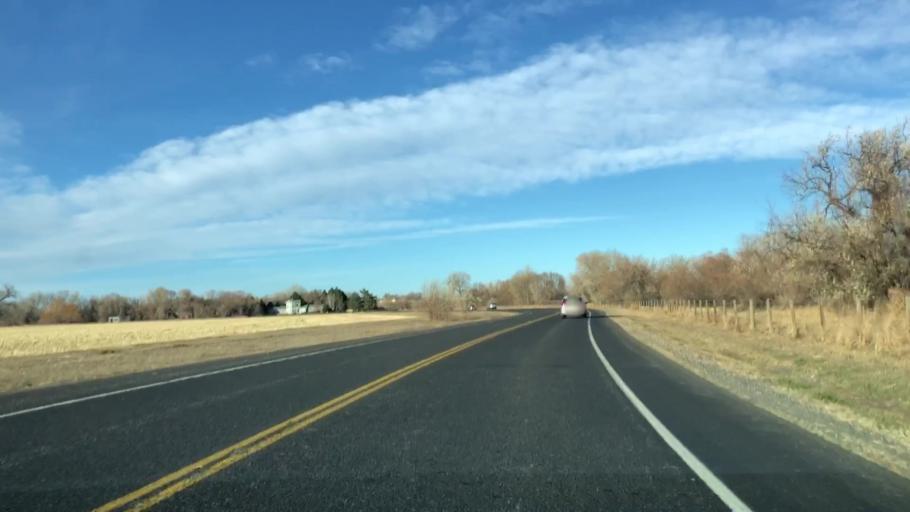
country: US
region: Colorado
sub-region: Weld County
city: Windsor
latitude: 40.5164
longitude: -104.9831
